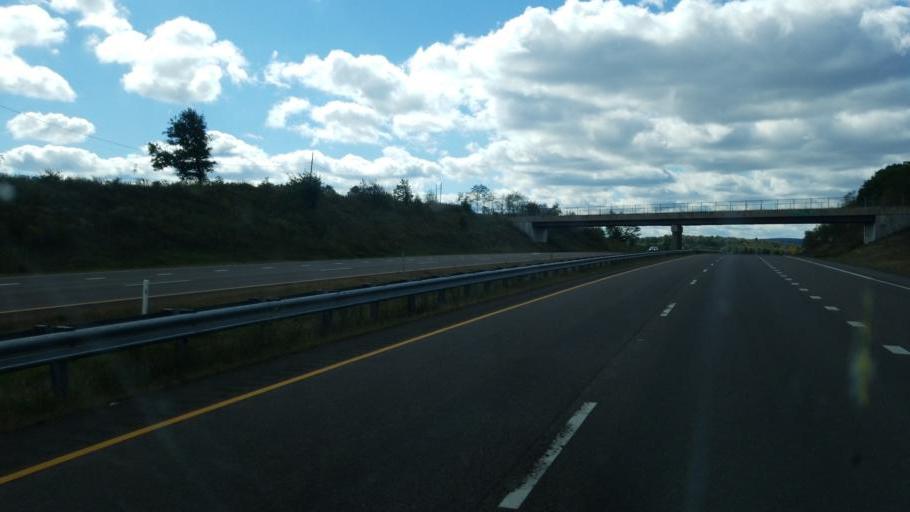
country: US
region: Maryland
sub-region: Allegany County
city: Frostburg
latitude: 39.6835
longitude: -79.0000
